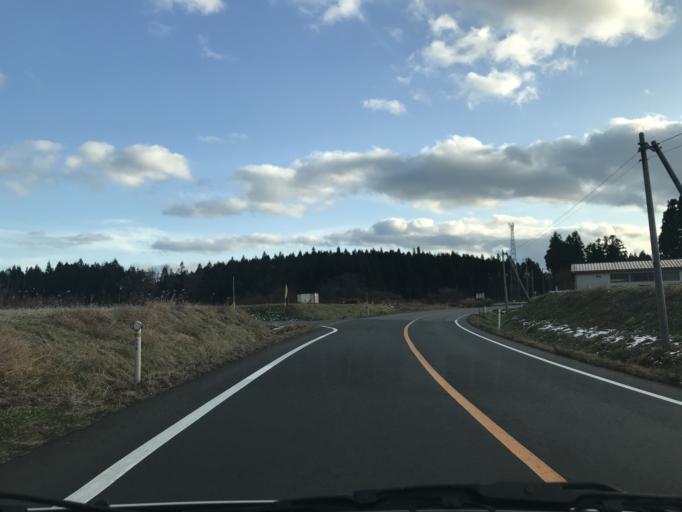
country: JP
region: Iwate
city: Mizusawa
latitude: 39.1608
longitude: 141.0527
